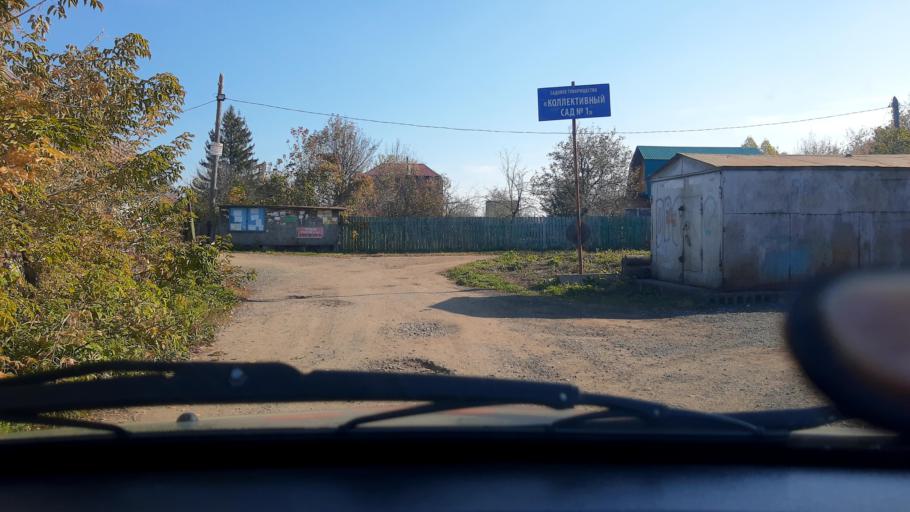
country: RU
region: Bashkortostan
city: Ufa
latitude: 54.8029
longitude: 56.1537
